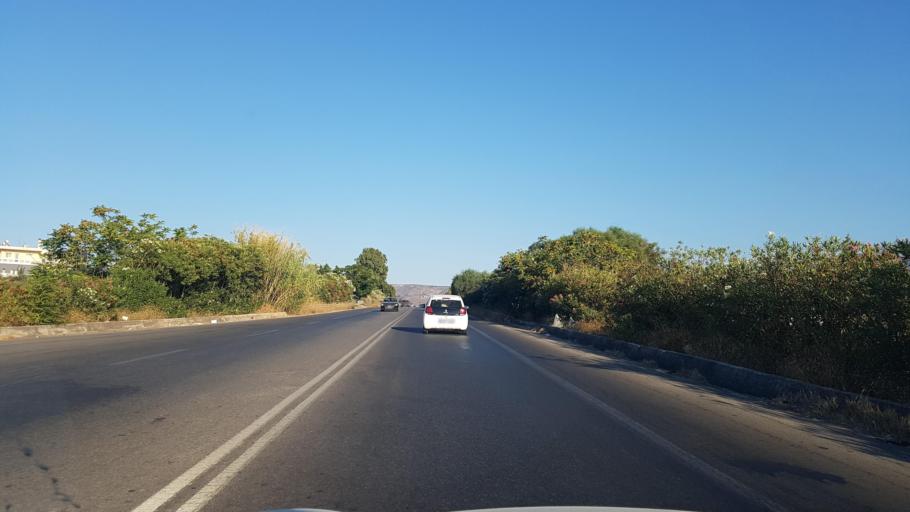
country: GR
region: Crete
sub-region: Nomos Chanias
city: Daratsos
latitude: 35.5031
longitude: 23.9836
